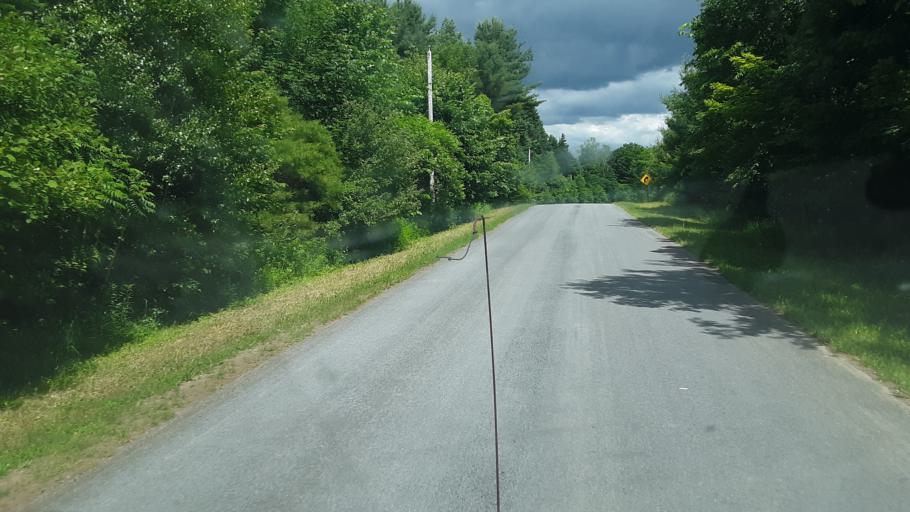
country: US
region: New York
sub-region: Oneida County
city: Rome
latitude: 43.3937
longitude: -75.5063
